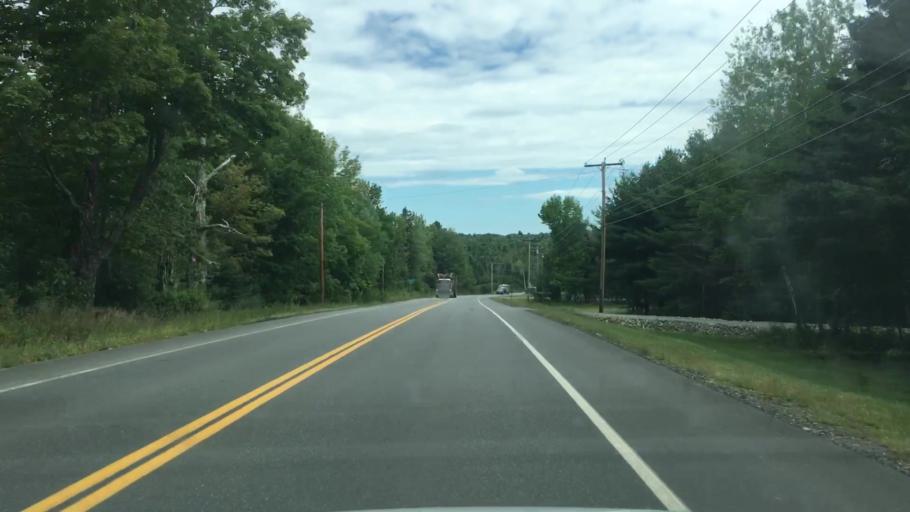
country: US
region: Maine
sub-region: Piscataquis County
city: Milo
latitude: 45.2412
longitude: -69.0391
